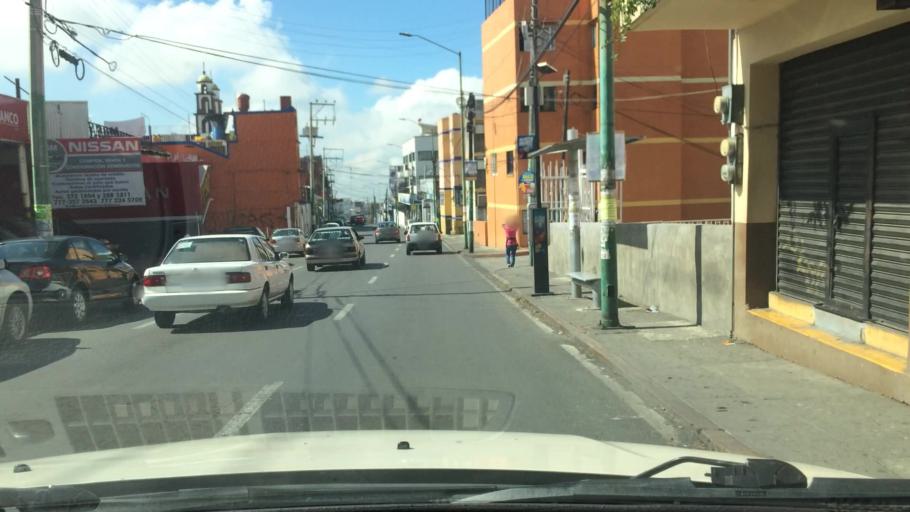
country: MX
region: Morelos
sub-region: Cuernavaca
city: Cuernavaca
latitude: 18.9399
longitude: -99.2415
